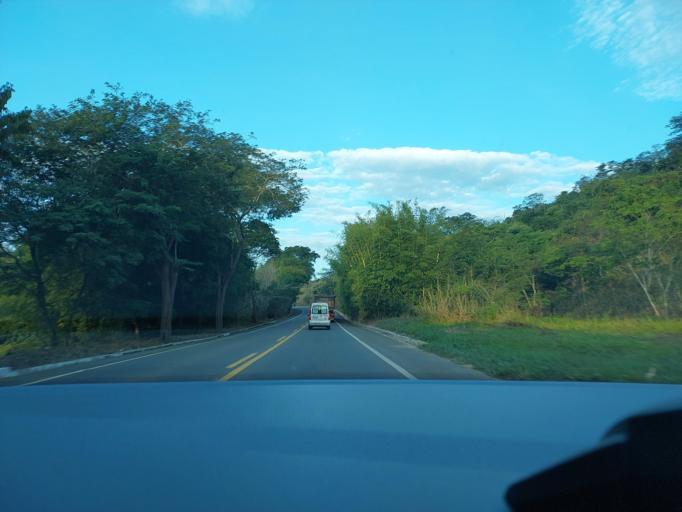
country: BR
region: Minas Gerais
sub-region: Muriae
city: Muriae
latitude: -21.1316
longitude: -42.1932
